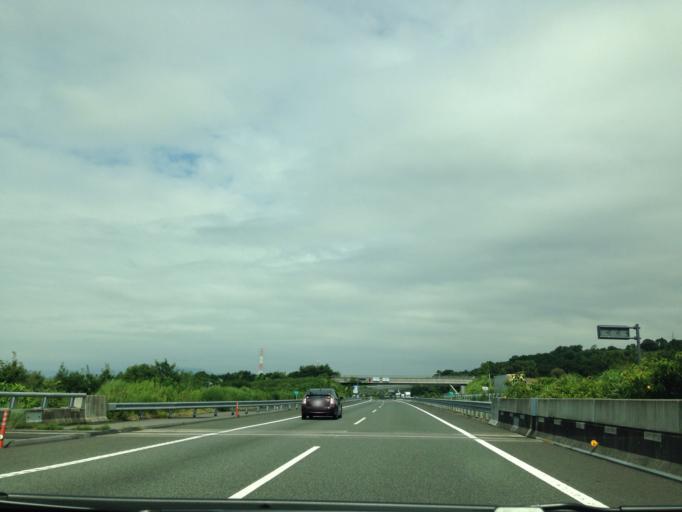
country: JP
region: Shizuoka
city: Fuji
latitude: 35.1589
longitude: 138.7770
